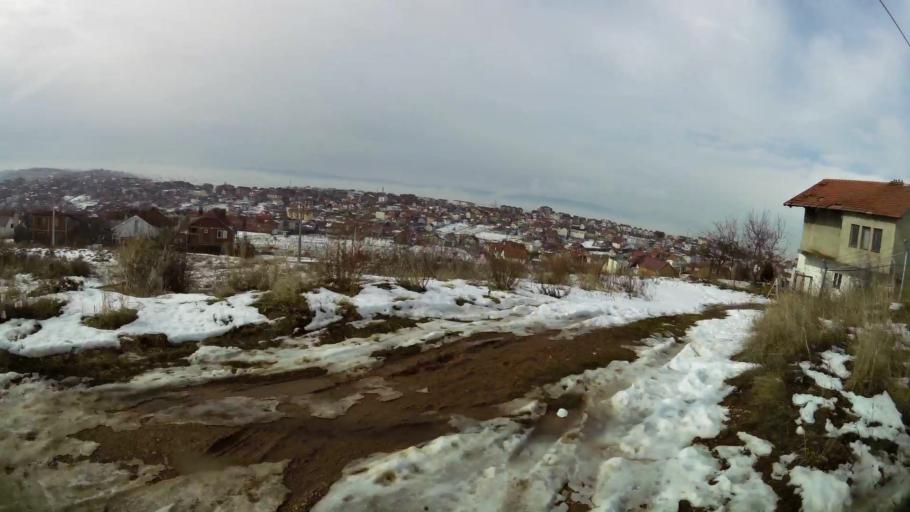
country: XK
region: Pristina
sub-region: Komuna e Prishtines
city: Pristina
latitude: 42.6863
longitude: 21.1688
